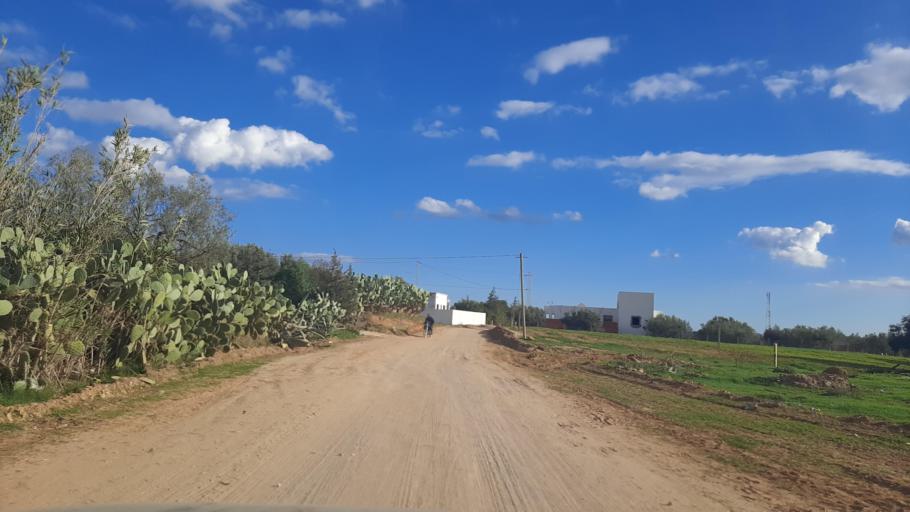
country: TN
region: Nabul
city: Al Hammamat
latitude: 36.4218
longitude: 10.5095
